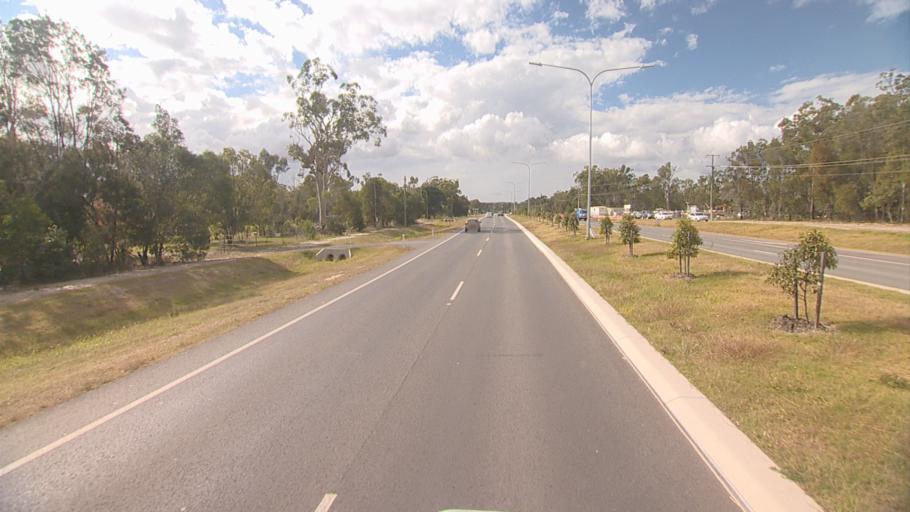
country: AU
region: Queensland
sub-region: Logan
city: Logan Reserve
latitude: -27.7029
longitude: 153.0971
